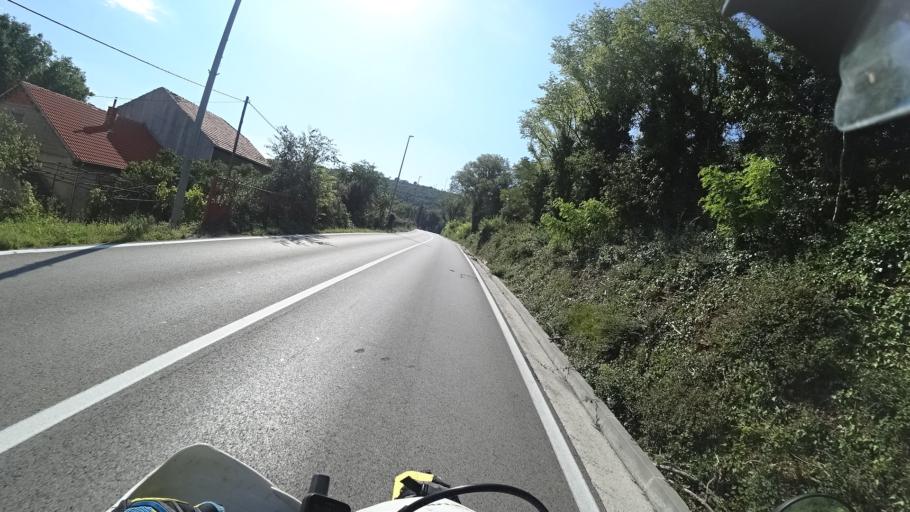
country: HR
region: Sibensko-Kniniska
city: Knin
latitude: 44.0291
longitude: 16.1927
